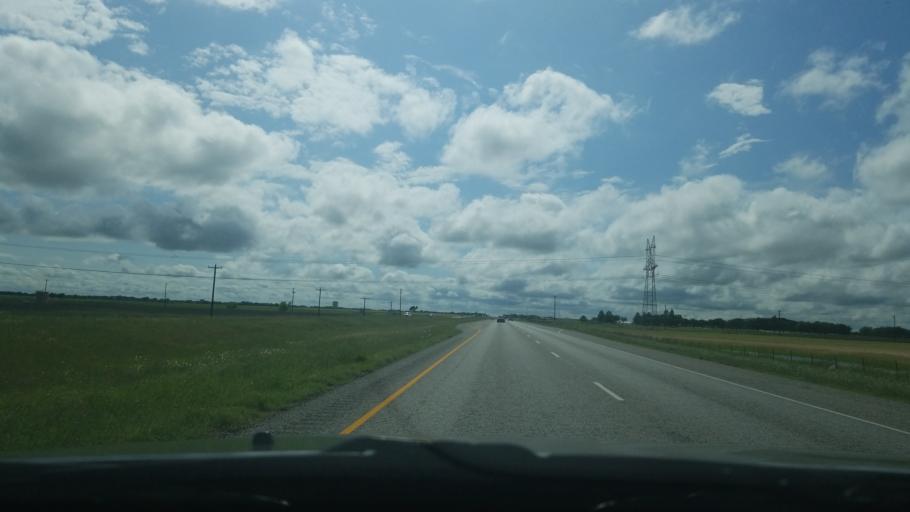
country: US
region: Texas
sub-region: Denton County
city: Ponder
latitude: 33.2370
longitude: -97.2898
